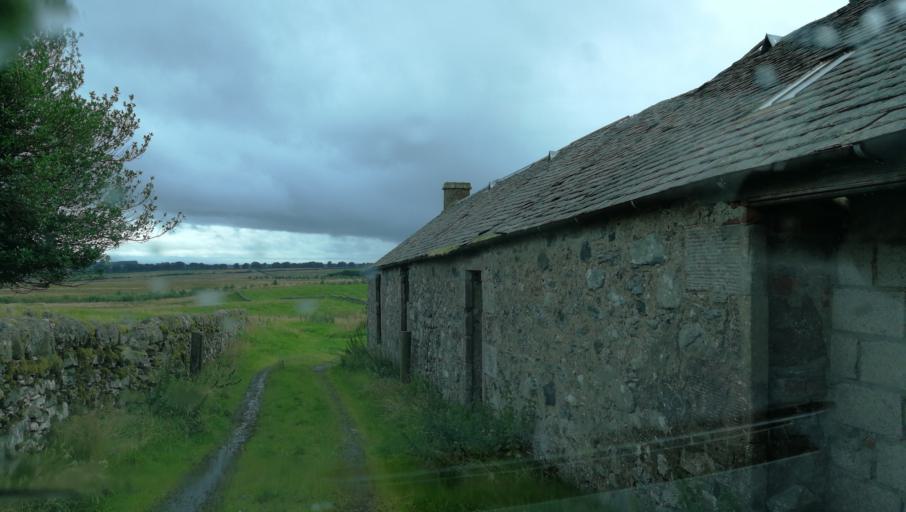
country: GB
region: Scotland
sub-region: Perth and Kinross
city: Blairgowrie
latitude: 56.6677
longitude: -3.3477
